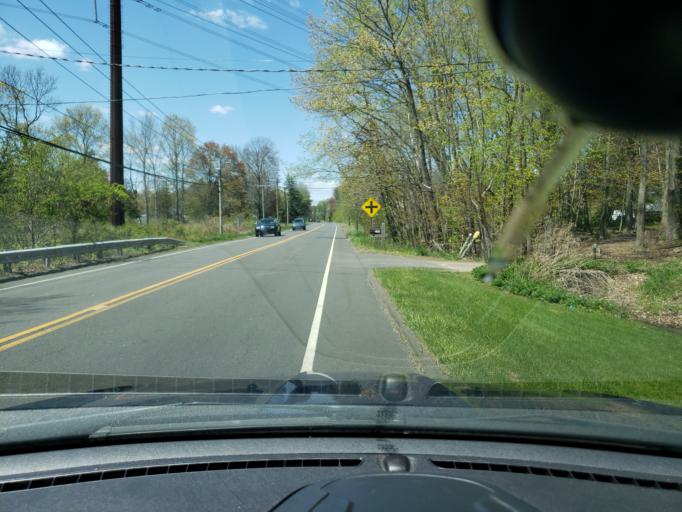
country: US
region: Connecticut
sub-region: New Haven County
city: Orange
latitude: 41.2830
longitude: -73.0099
